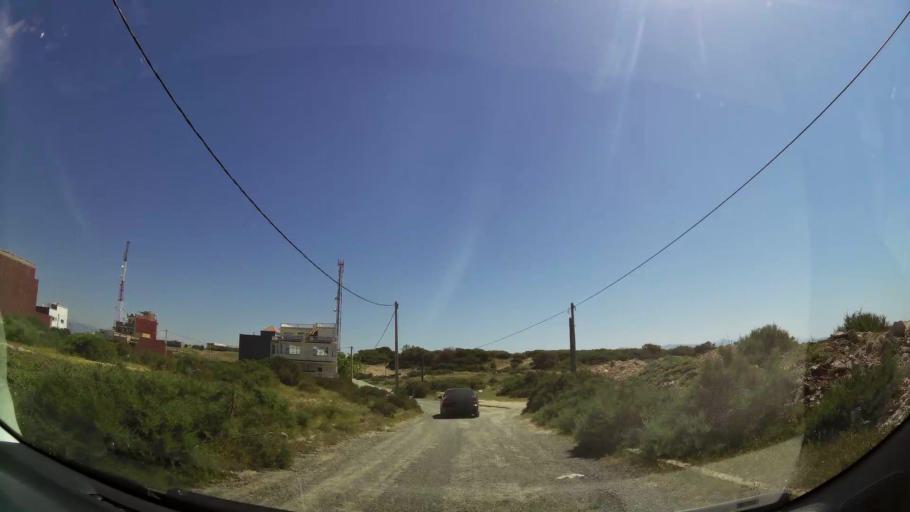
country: MA
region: Oriental
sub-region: Berkane-Taourirt
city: Madagh
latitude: 35.1434
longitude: -2.4272
